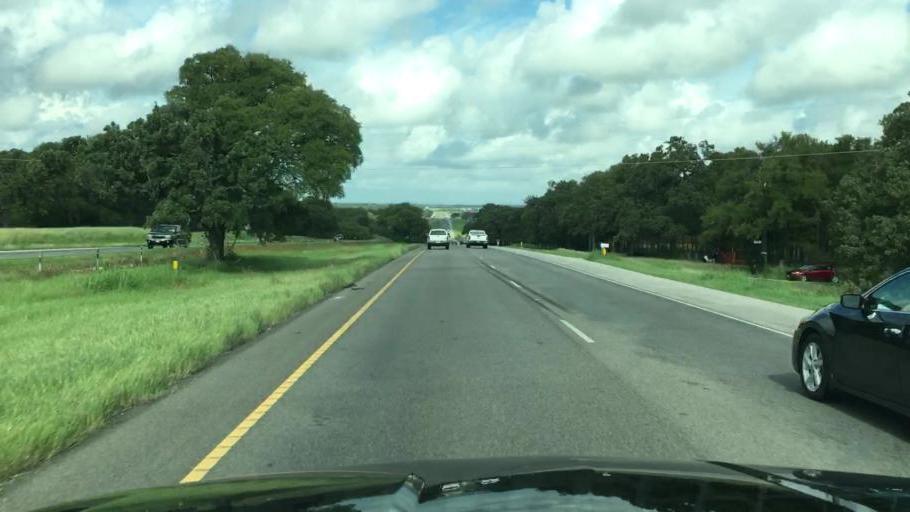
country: US
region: Texas
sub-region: Bastrop County
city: Wyldwood
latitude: 30.1526
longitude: -97.4904
